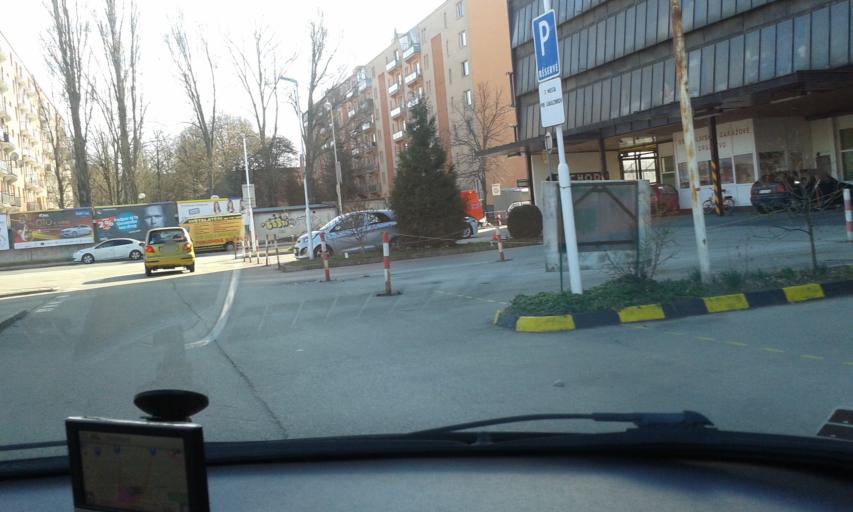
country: SK
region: Bratislavsky
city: Bratislava
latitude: 48.1616
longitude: 17.1594
